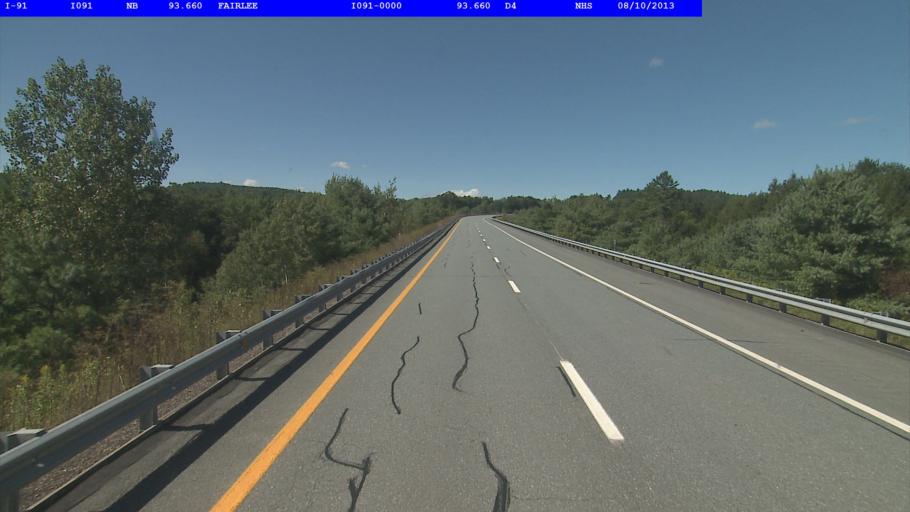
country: US
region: New Hampshire
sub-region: Grafton County
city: Orford
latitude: 43.9283
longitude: -72.1336
